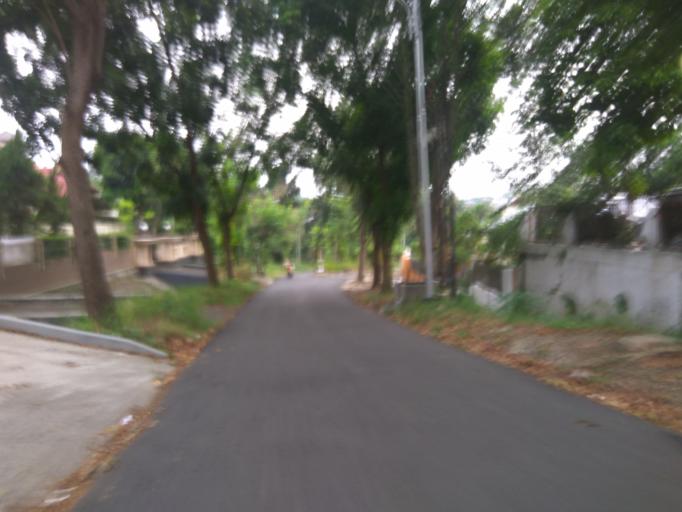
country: ID
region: Central Java
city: Semarang
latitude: -7.0074
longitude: 110.4136
